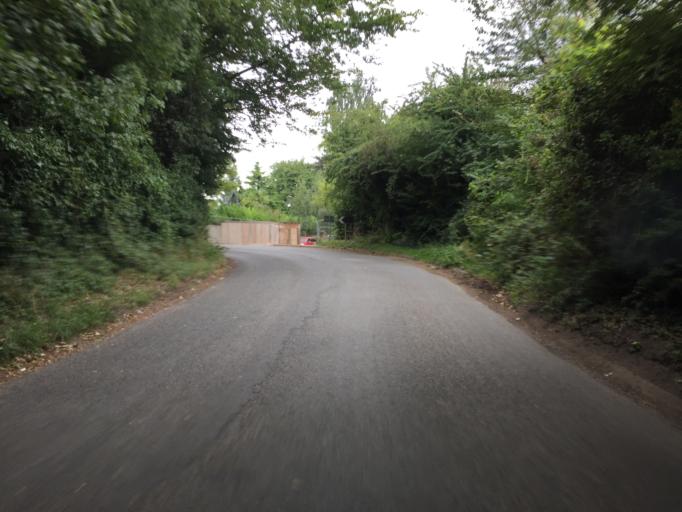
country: GB
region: England
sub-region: Kent
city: Maidstone
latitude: 51.2405
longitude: 0.5321
